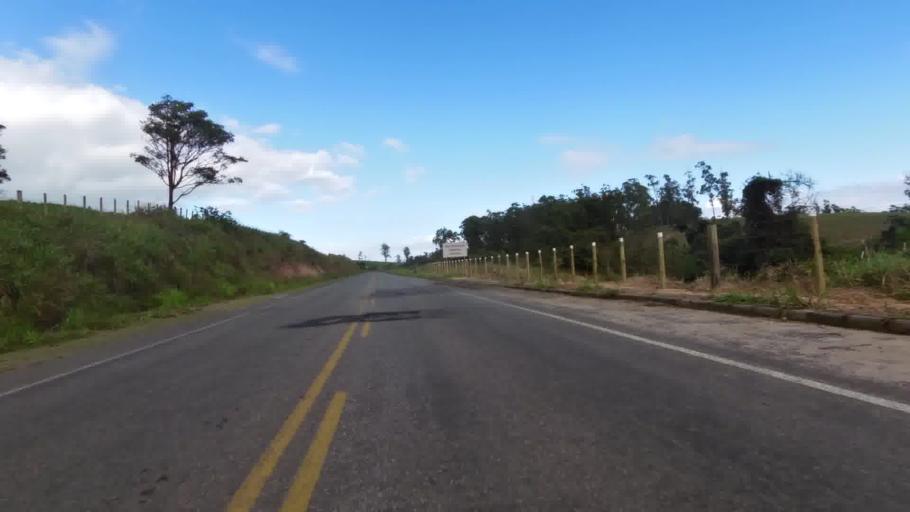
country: BR
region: Espirito Santo
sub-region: Piuma
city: Piuma
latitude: -20.7935
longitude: -40.6080
